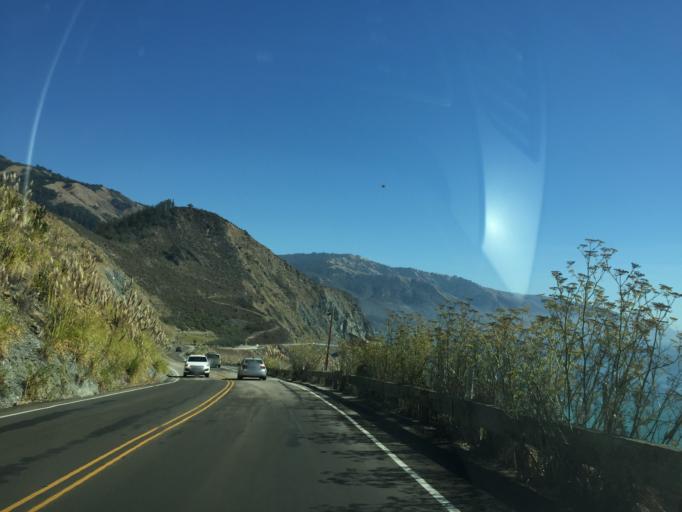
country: US
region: California
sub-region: Monterey County
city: Greenfield
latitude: 36.0160
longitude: -121.5332
